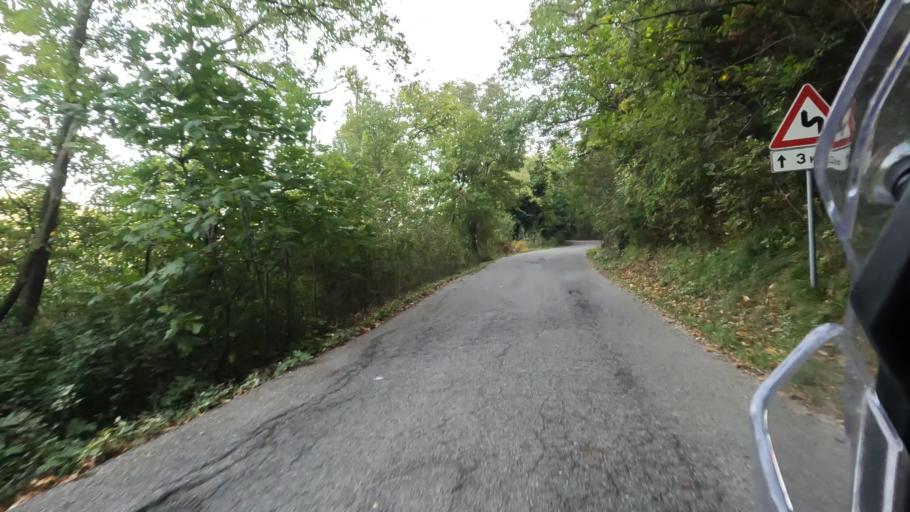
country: IT
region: Liguria
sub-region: Provincia di Savona
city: San Giovanni
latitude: 44.3947
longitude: 8.5357
